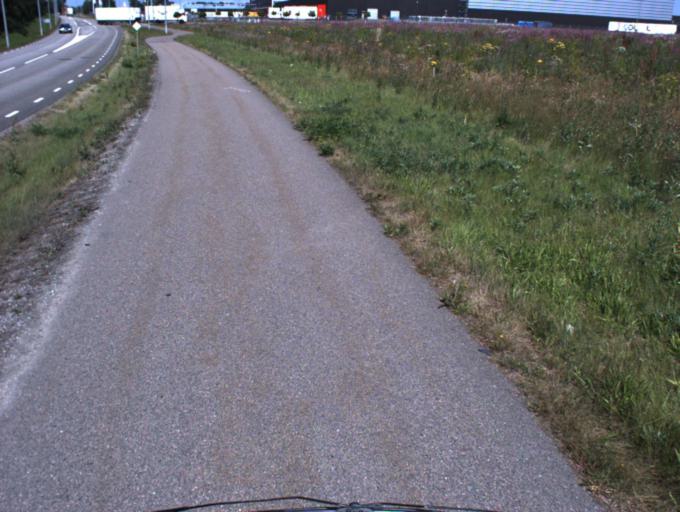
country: SE
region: Skane
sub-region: Helsingborg
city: Barslov
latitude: 56.0343
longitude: 12.7809
